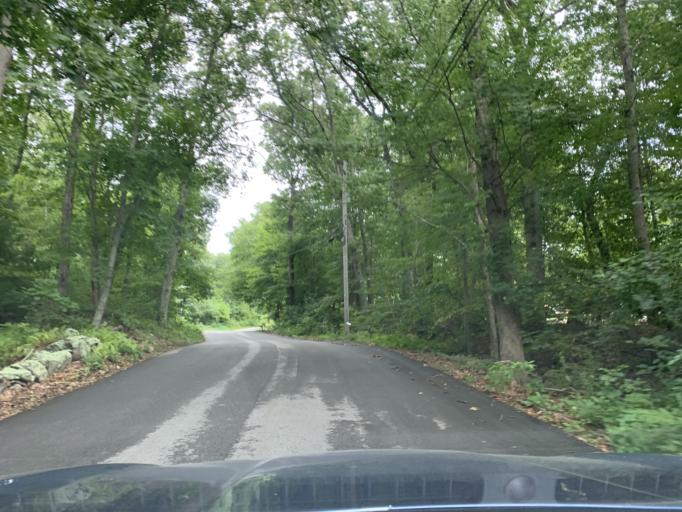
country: US
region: Rhode Island
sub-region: Kent County
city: West Warwick
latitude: 41.7427
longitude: -71.5961
